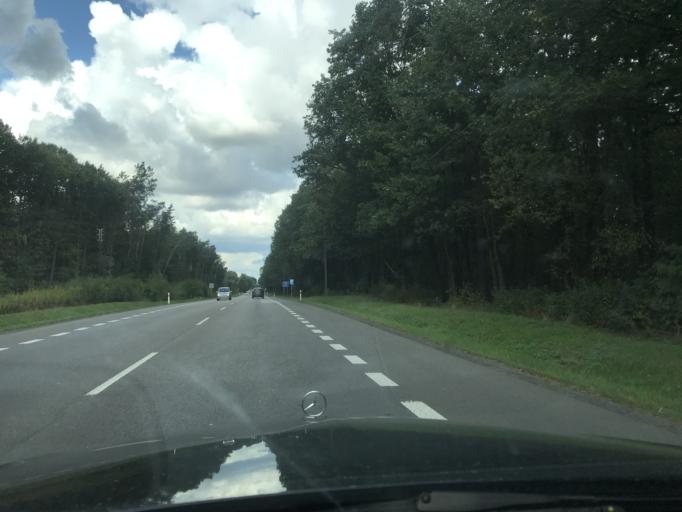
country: PL
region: Lublin Voivodeship
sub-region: Powiat lubelski
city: Niemce
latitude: 51.3788
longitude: 22.6350
